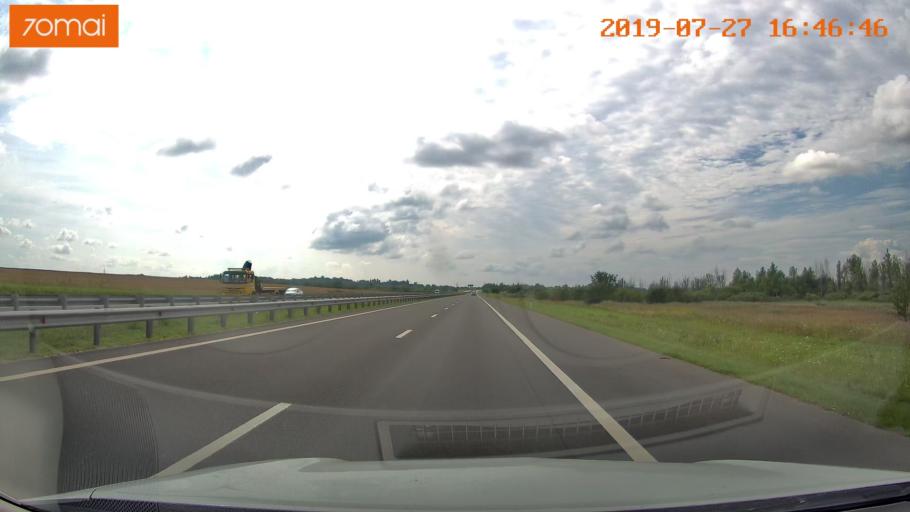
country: RU
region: Kaliningrad
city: Gvardeysk
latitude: 54.6676
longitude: 21.0127
